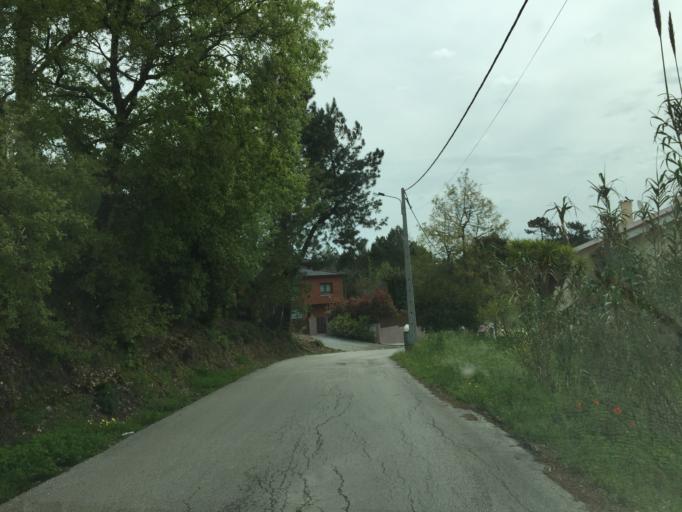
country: PT
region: Leiria
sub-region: Leiria
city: Caranguejeira
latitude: 39.7856
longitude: -8.7411
